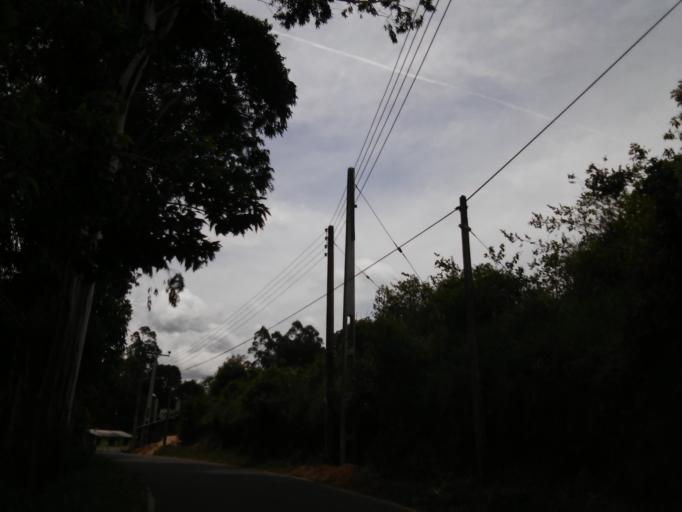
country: LK
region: Uva
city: Haputale
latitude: 6.8497
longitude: 81.0260
